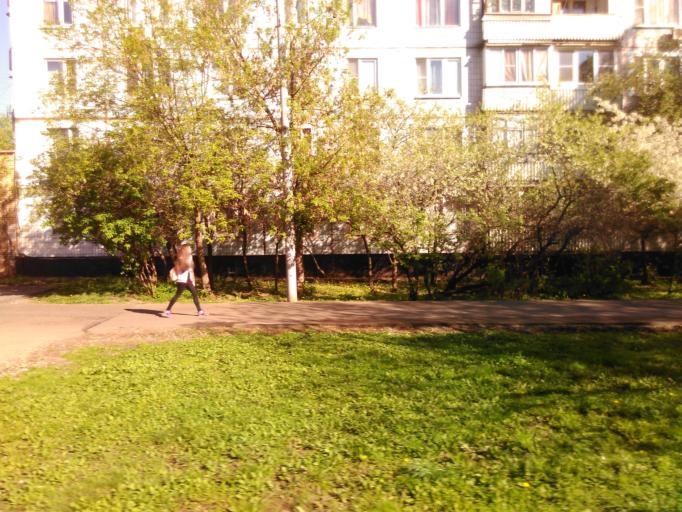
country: RU
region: Moskovskaya
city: Koptevo
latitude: 55.8216
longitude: 37.5119
